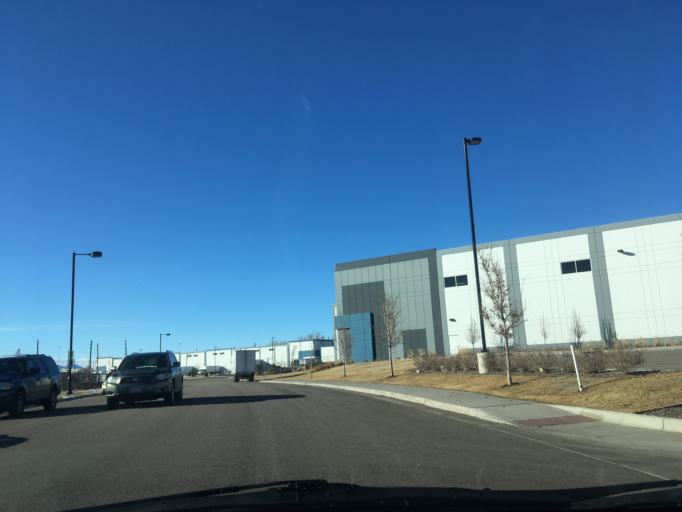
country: US
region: Colorado
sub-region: Adams County
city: Twin Lakes
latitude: 39.7941
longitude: -104.9826
